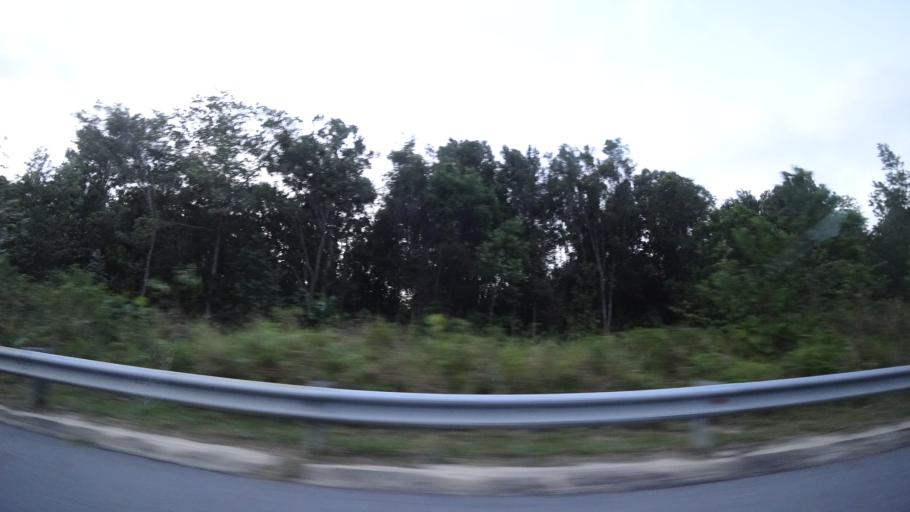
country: BN
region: Brunei and Muara
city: Bandar Seri Begawan
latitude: 4.9224
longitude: 114.8082
